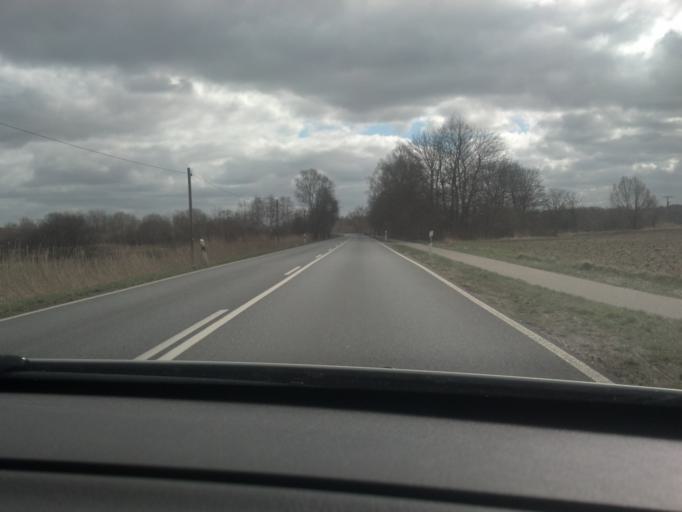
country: DE
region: Mecklenburg-Vorpommern
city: Rechlin
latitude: 53.3208
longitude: 12.7038
